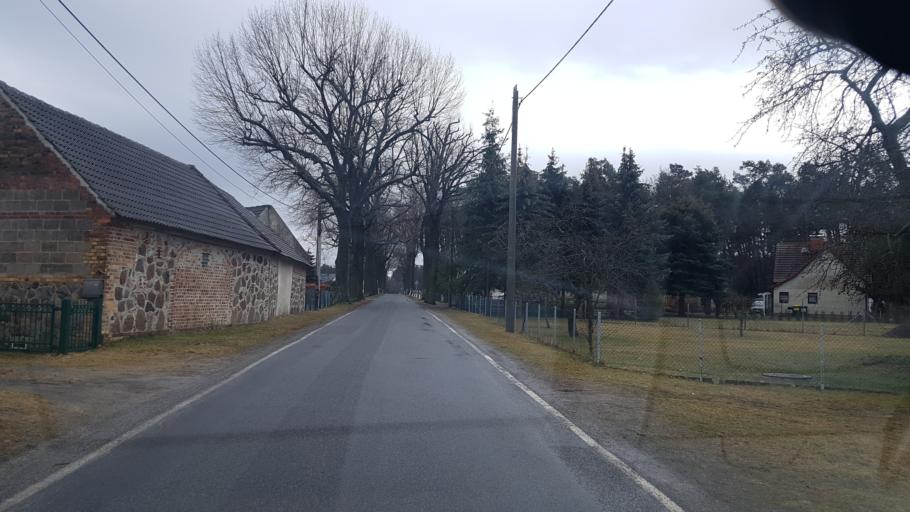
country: DE
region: Brandenburg
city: Neupetershain
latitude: 51.6197
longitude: 14.1065
